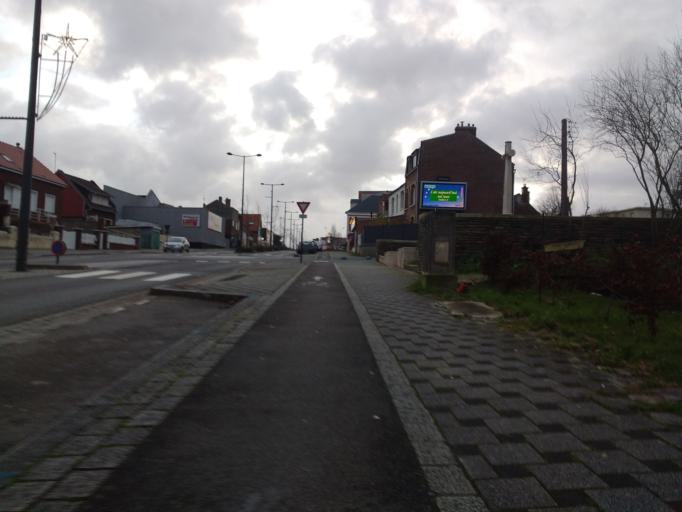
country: FR
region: Picardie
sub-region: Departement de la Somme
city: Longueau
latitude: 49.8697
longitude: 2.3592
